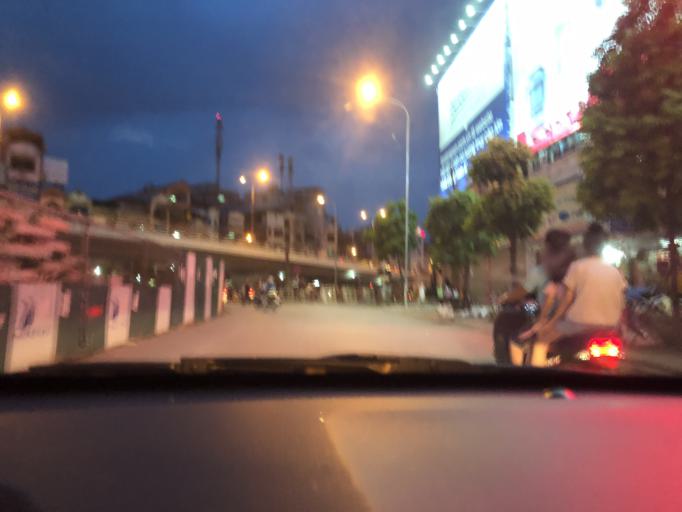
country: VN
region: Ha Noi
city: Hai BaTrung
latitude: 20.9974
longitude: 105.8407
